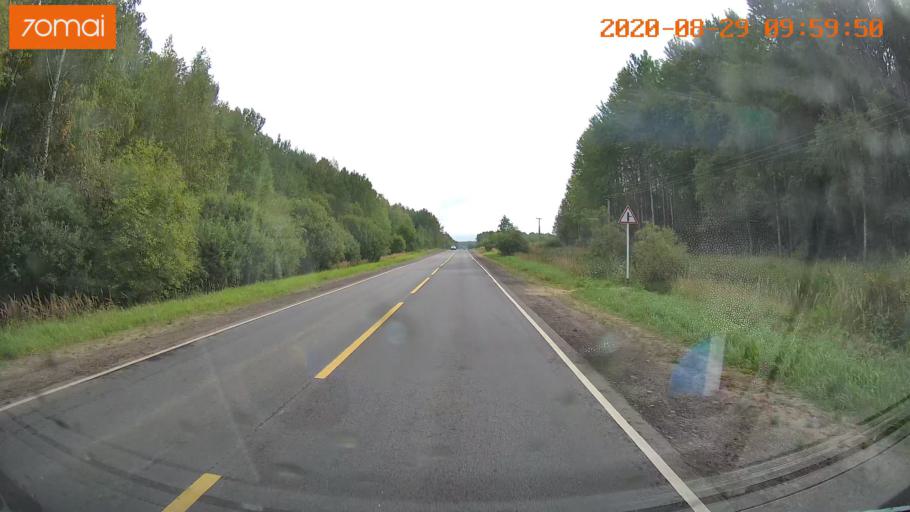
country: RU
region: Ivanovo
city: Zarechnyy
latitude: 57.4105
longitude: 42.3769
